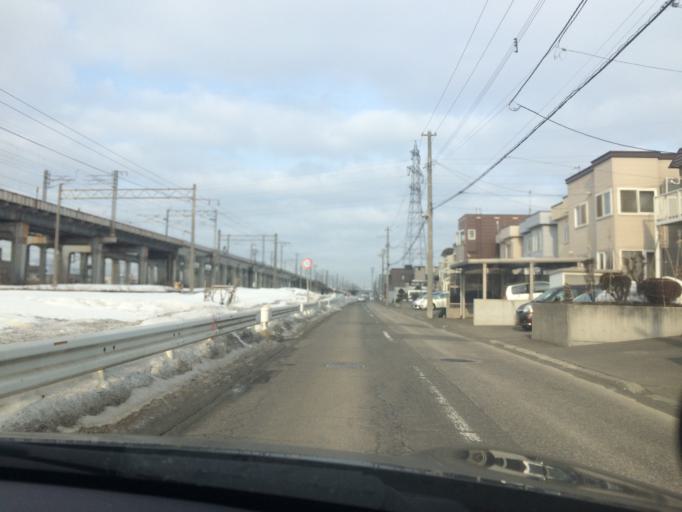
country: JP
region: Hokkaido
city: Sapporo
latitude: 43.0440
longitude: 141.4536
